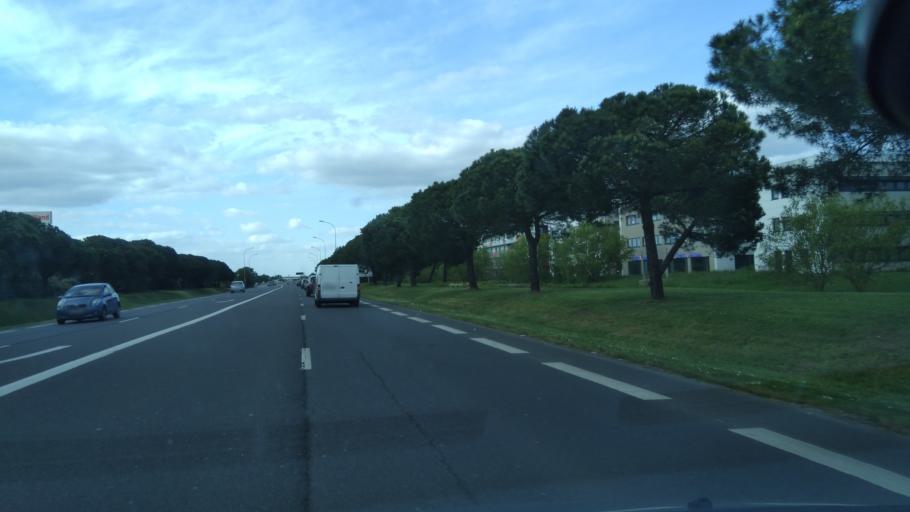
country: FR
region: Pays de la Loire
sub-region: Departement de la Loire-Atlantique
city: Saint-Nazaire
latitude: 47.2956
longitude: -2.2078
